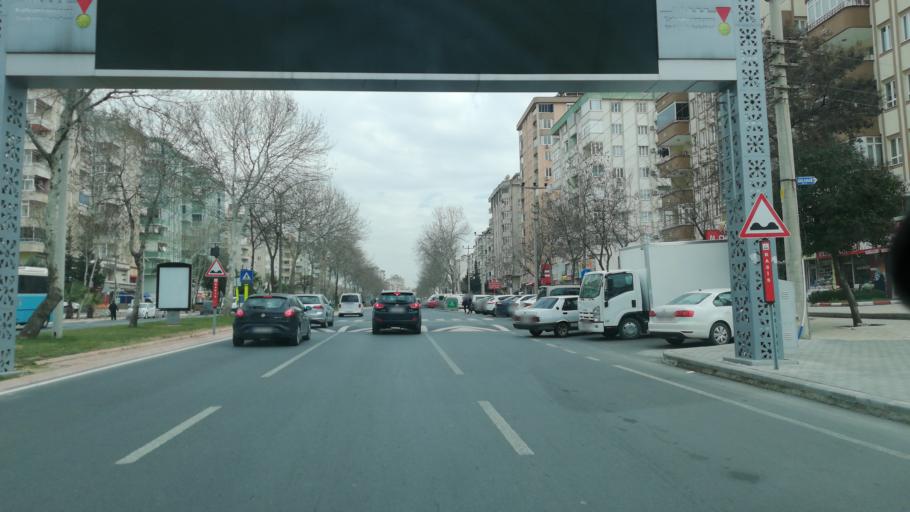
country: TR
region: Kahramanmaras
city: Kahramanmaras
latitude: 37.5887
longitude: 36.8822
